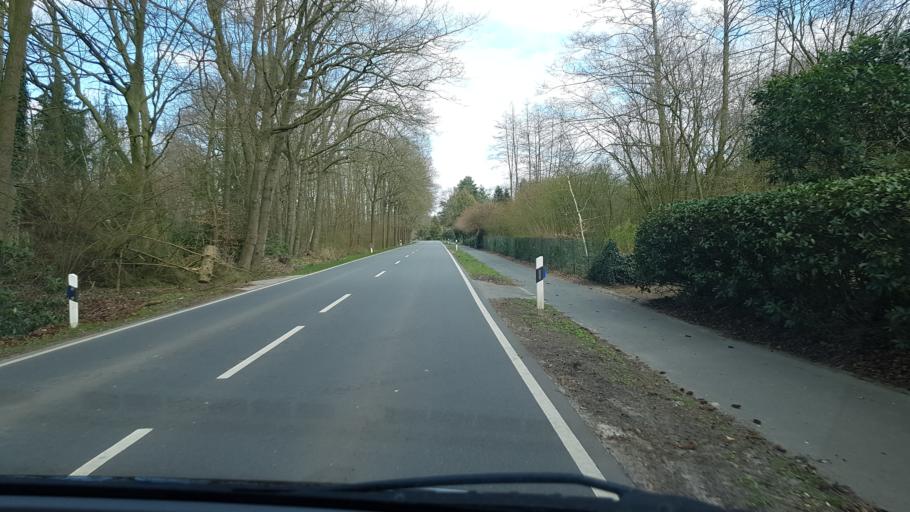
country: DE
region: Lower Saxony
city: Edewecht
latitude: 53.1508
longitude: 7.9431
